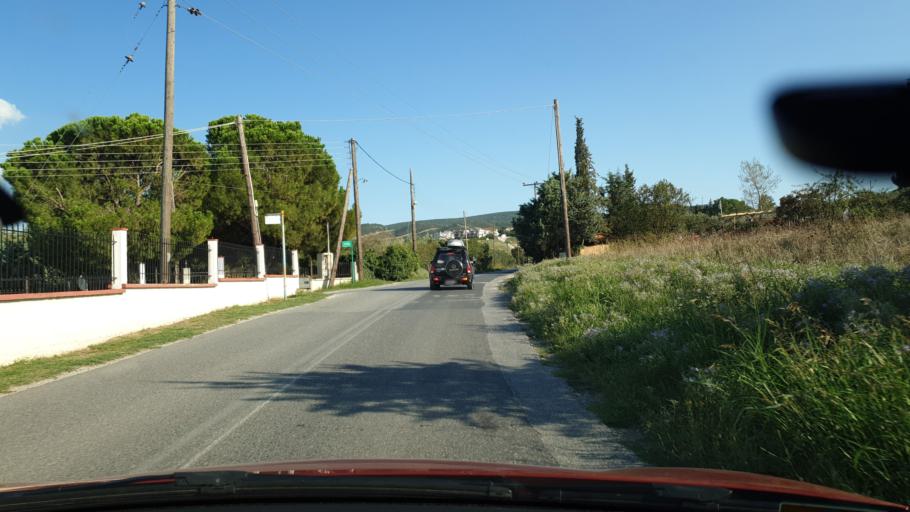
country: GR
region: Central Macedonia
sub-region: Nomos Thessalonikis
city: Agia Paraskevi
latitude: 40.4871
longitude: 23.0409
